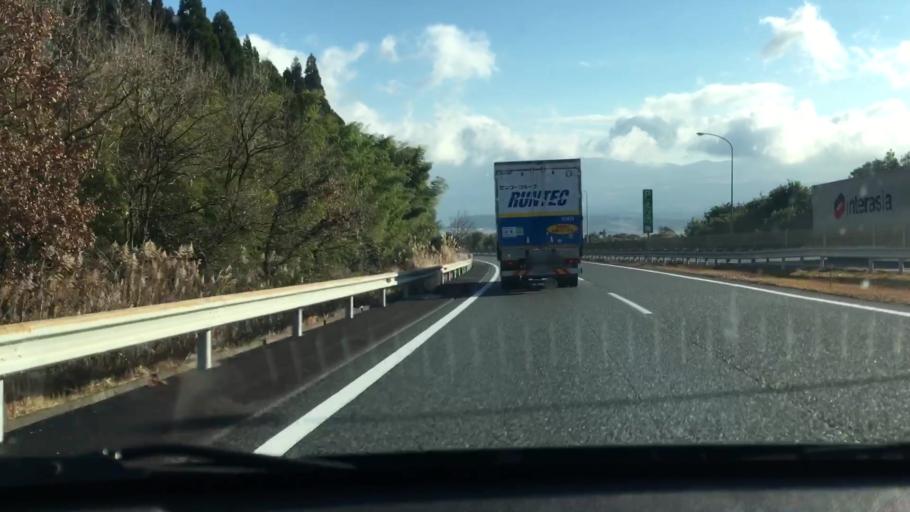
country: JP
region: Kumamoto
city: Hitoyoshi
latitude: 32.0729
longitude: 130.7935
